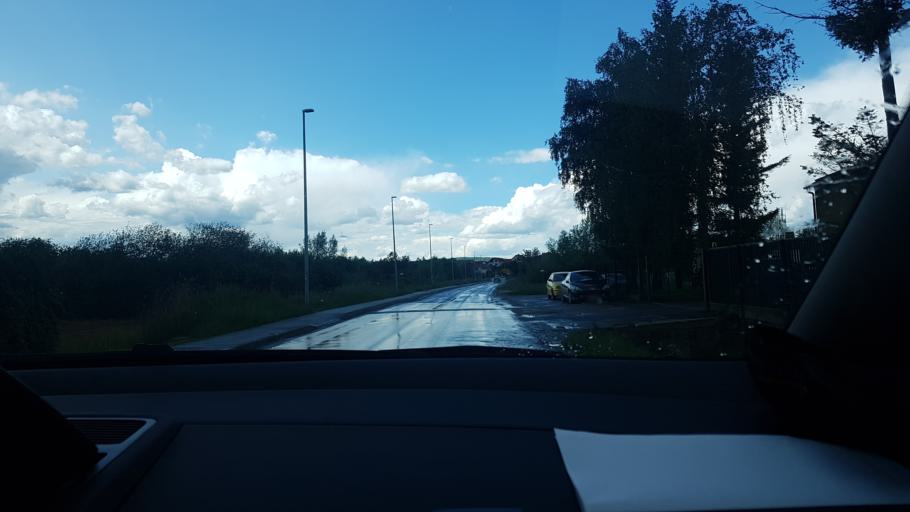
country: HR
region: Varazdinska
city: Ivanec
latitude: 46.2341
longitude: 16.1190
